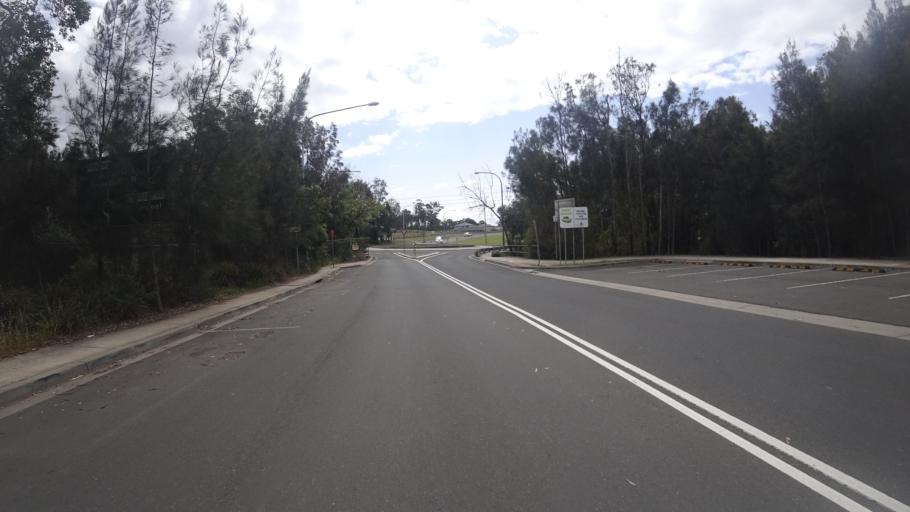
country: AU
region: New South Wales
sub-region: Campbelltown Municipality
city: Glenfield
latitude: -33.9681
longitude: 150.8967
